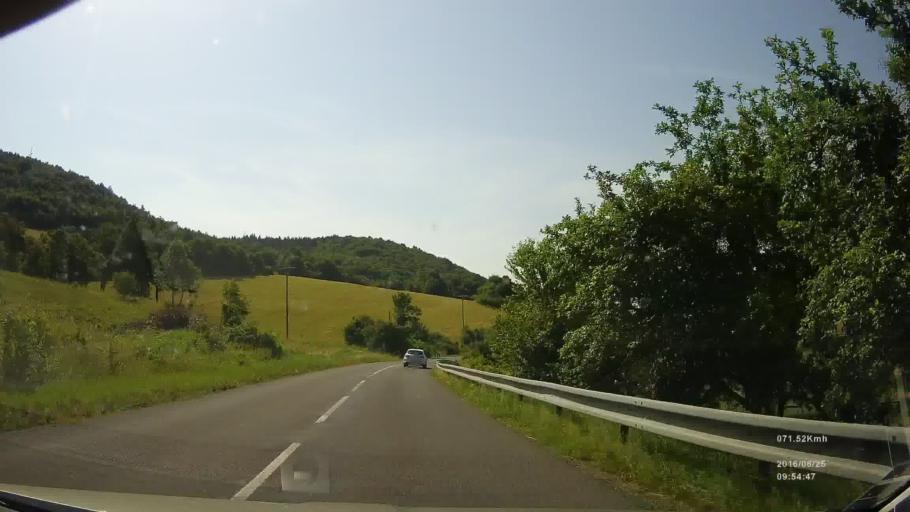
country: SK
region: Banskobystricky
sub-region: Okres Banska Bystrica
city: Banska Bystrica
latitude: 48.6928
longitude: 19.2186
